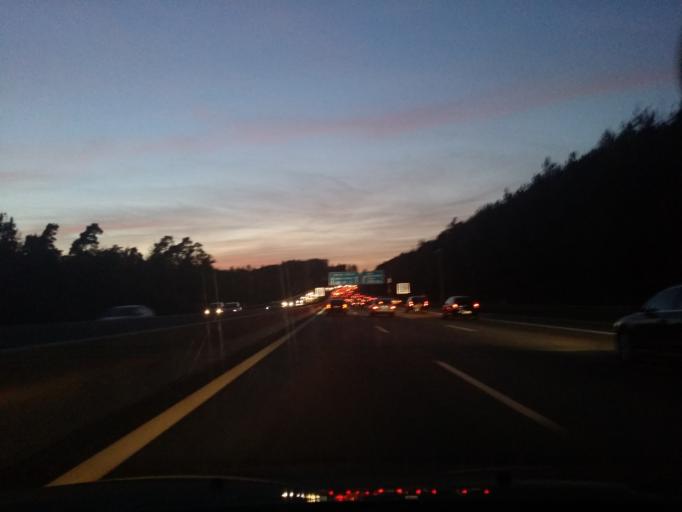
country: DE
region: Baden-Wuerttemberg
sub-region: Regierungsbezirk Stuttgart
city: Steinenbronn
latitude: 48.7131
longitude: 9.0959
